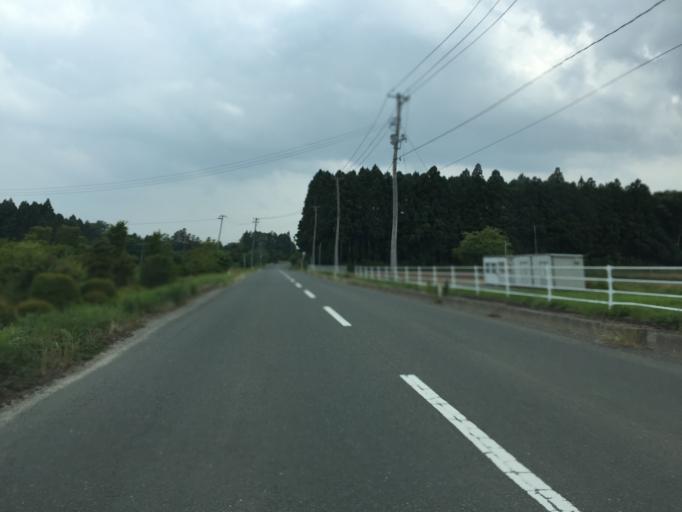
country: JP
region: Miyagi
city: Marumori
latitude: 37.8705
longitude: 140.8873
